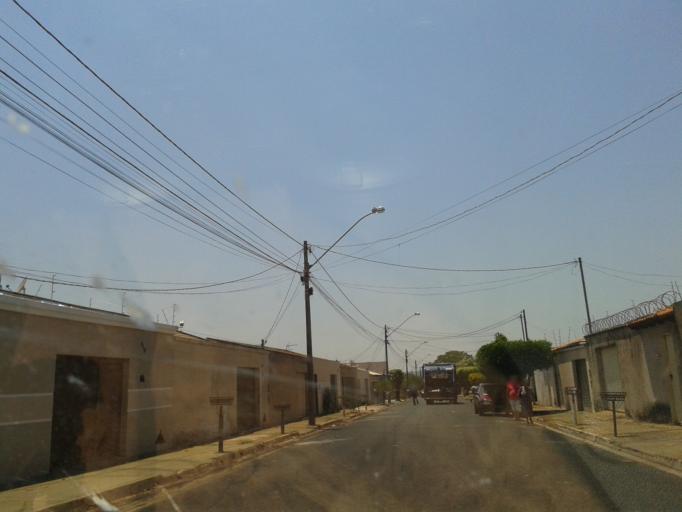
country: BR
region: Minas Gerais
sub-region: Uberlandia
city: Uberlandia
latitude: -18.9607
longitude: -48.3139
